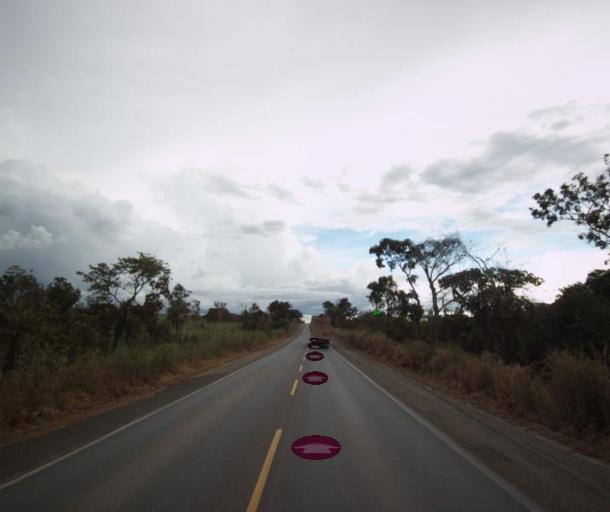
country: BR
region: Goias
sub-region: Itapaci
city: Itapaci
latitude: -14.9292
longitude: -49.3649
